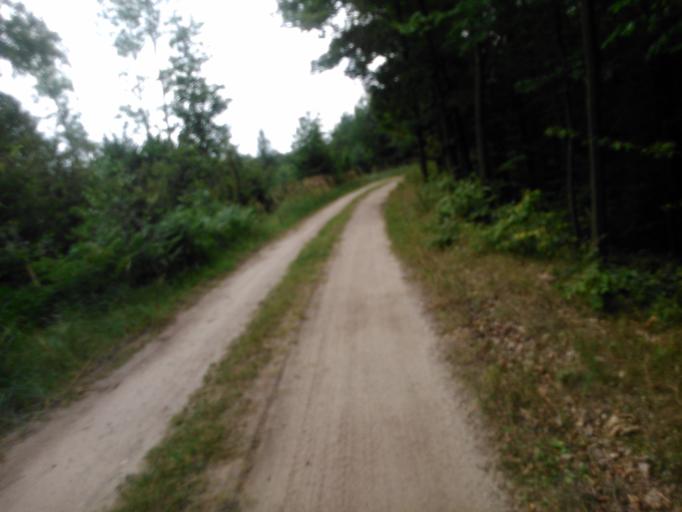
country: PL
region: Kujawsko-Pomorskie
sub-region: Powiat brodnicki
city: Gorzno
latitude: 53.2097
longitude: 19.7139
